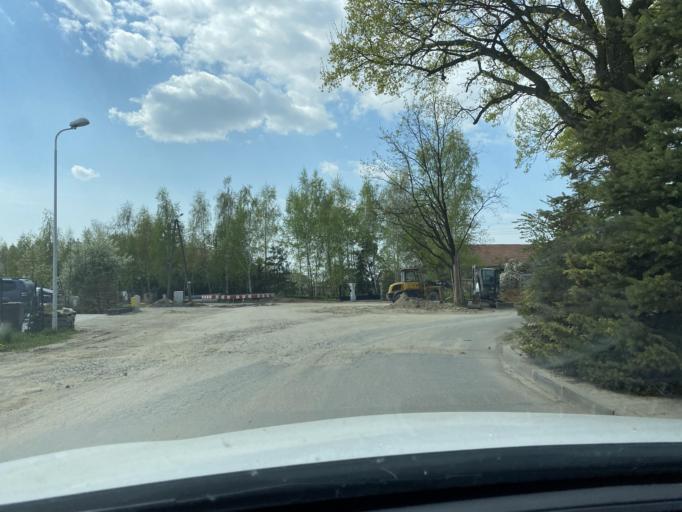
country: PL
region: Lower Silesian Voivodeship
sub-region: Powiat wroclawski
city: Mirkow
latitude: 51.1589
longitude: 17.1734
